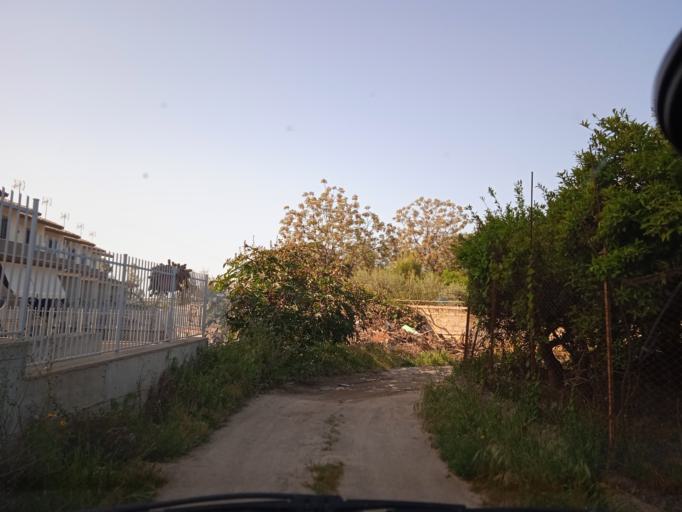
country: IT
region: Sicily
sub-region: Palermo
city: Villabate
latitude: 38.0817
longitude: 13.4515
